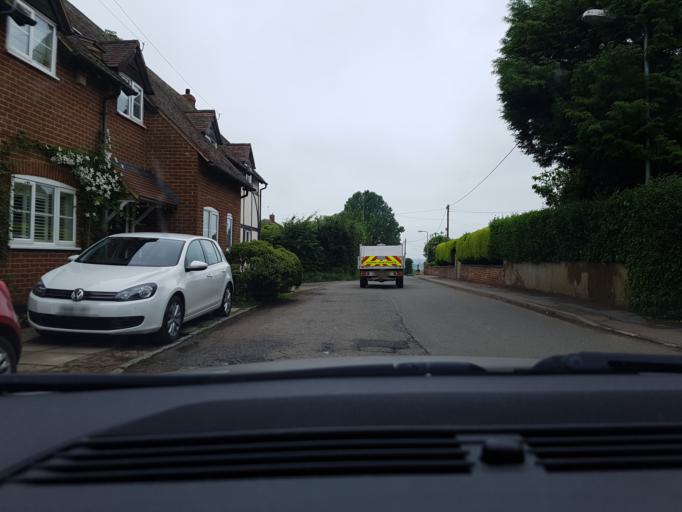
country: GB
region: England
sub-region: Buckinghamshire
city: Steeple Claydon
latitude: 51.9362
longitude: -0.9810
